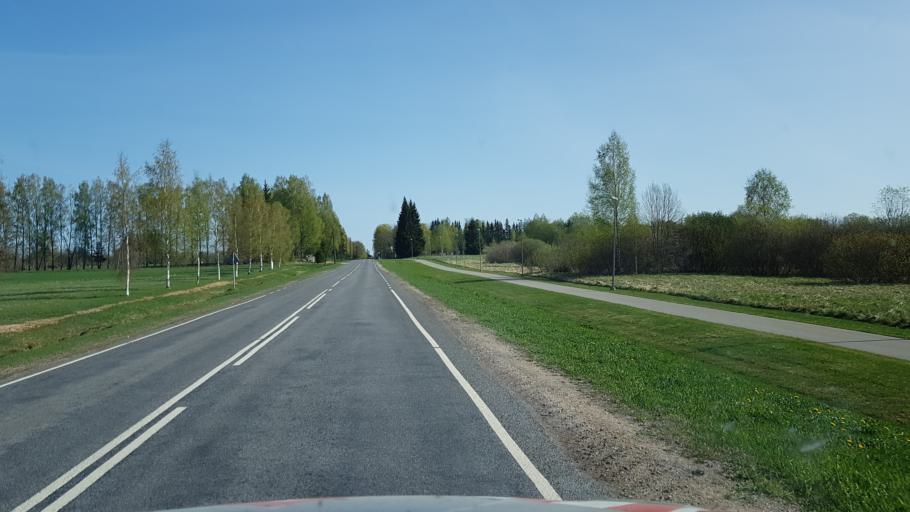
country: EE
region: Viljandimaa
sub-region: Abja vald
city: Abja-Paluoja
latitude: 58.1575
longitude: 25.4324
